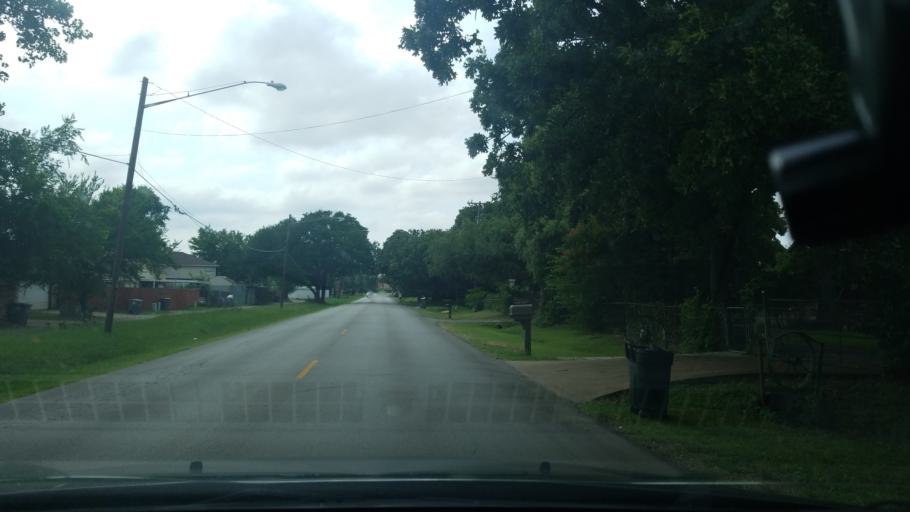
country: US
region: Texas
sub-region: Dallas County
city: Balch Springs
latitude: 32.7569
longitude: -96.6406
